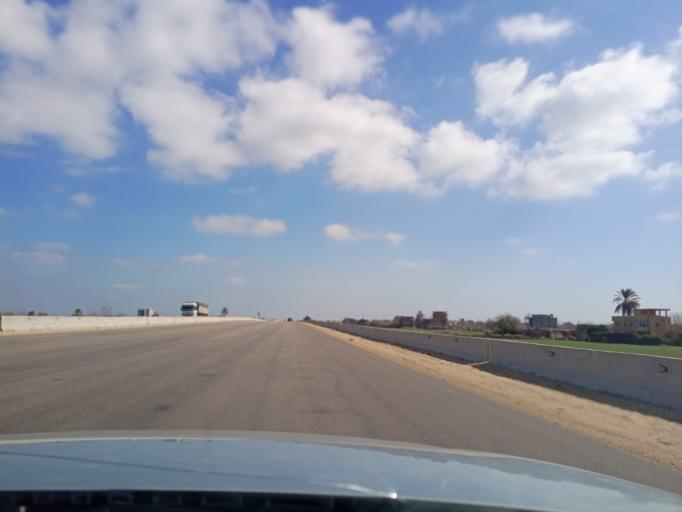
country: EG
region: Muhafazat al Minufiyah
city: Al Bajur
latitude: 30.3985
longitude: 31.0186
